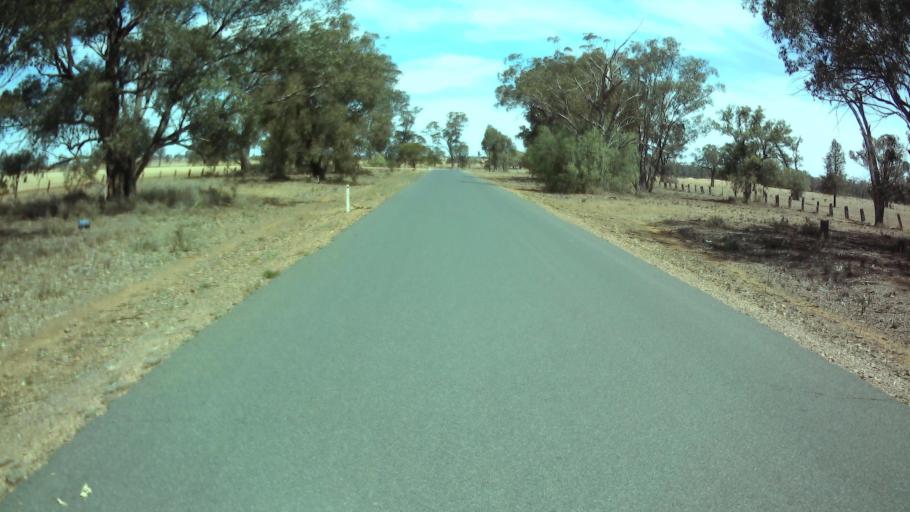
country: AU
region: New South Wales
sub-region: Weddin
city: Grenfell
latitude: -33.8566
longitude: 147.7461
